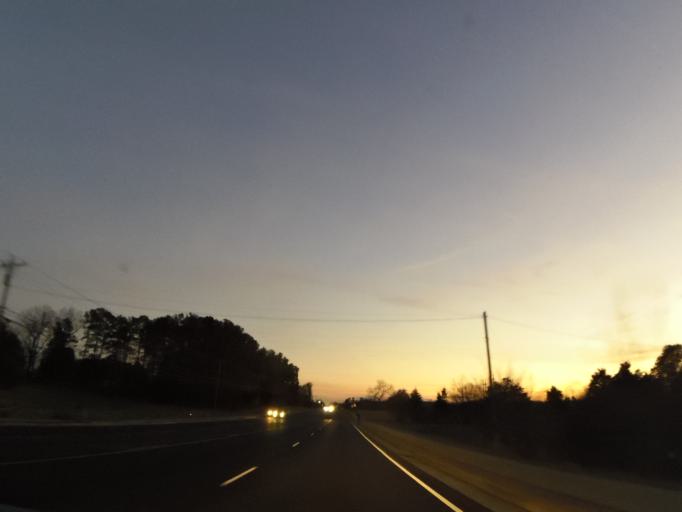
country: US
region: Georgia
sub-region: Whitfield County
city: Varnell
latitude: 34.8680
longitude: -84.9445
